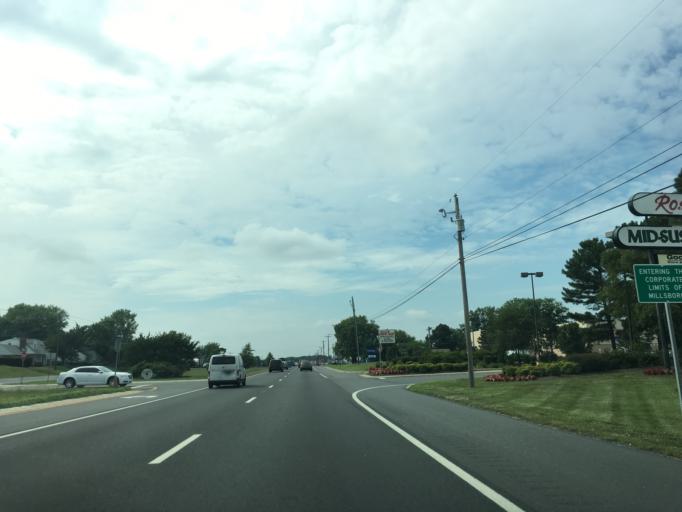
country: US
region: Delaware
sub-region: Sussex County
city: Millsboro
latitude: 38.5785
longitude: -75.2888
